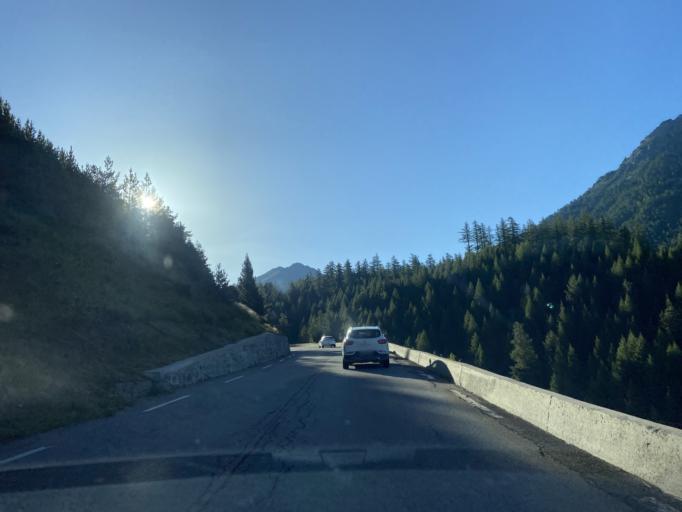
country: IT
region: Piedmont
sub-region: Provincia di Torino
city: Claviere
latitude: 44.9270
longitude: 6.7058
